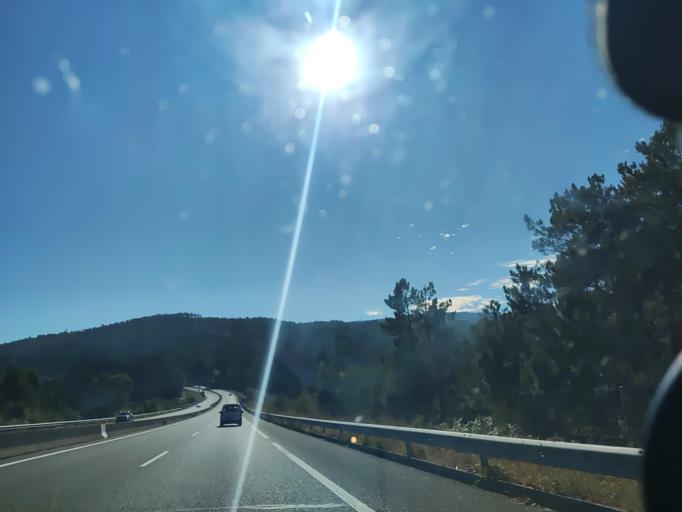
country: ES
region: Galicia
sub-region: Provincia da Coruna
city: Boiro
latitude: 42.6586
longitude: -8.8934
